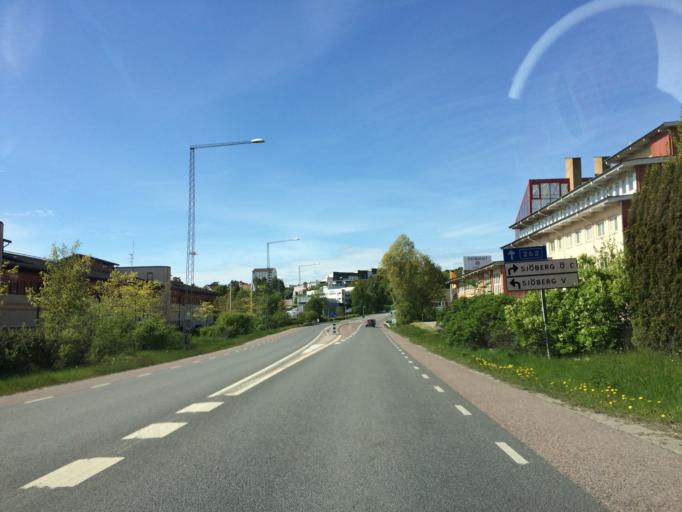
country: SE
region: Stockholm
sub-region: Sollentuna Kommun
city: Sollentuna
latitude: 59.4254
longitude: 17.9997
